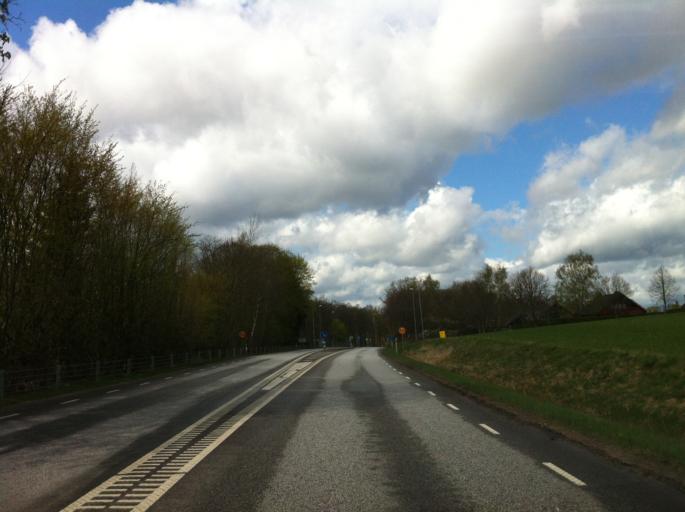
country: SE
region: Skane
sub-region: Hoors Kommun
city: Satofta
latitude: 55.9305
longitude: 13.5655
